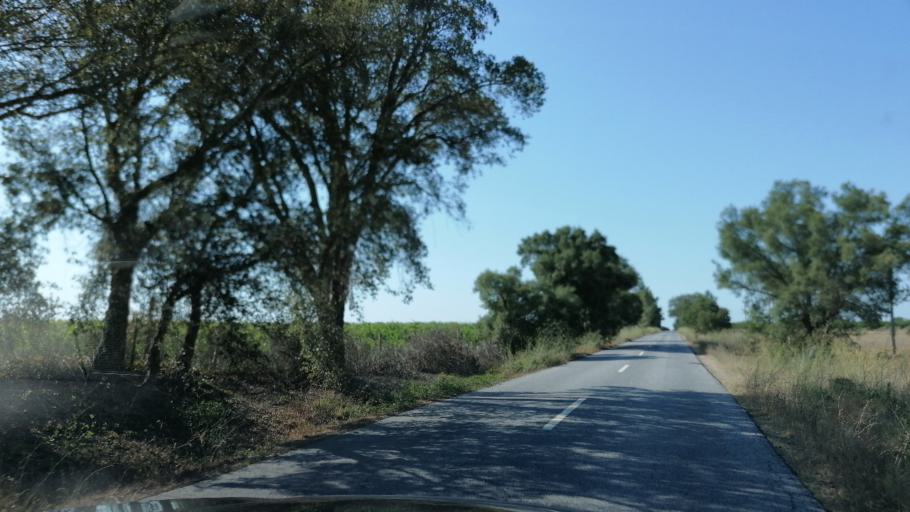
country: PT
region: Evora
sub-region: Vendas Novas
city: Vendas Novas
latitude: 38.7386
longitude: -8.6264
